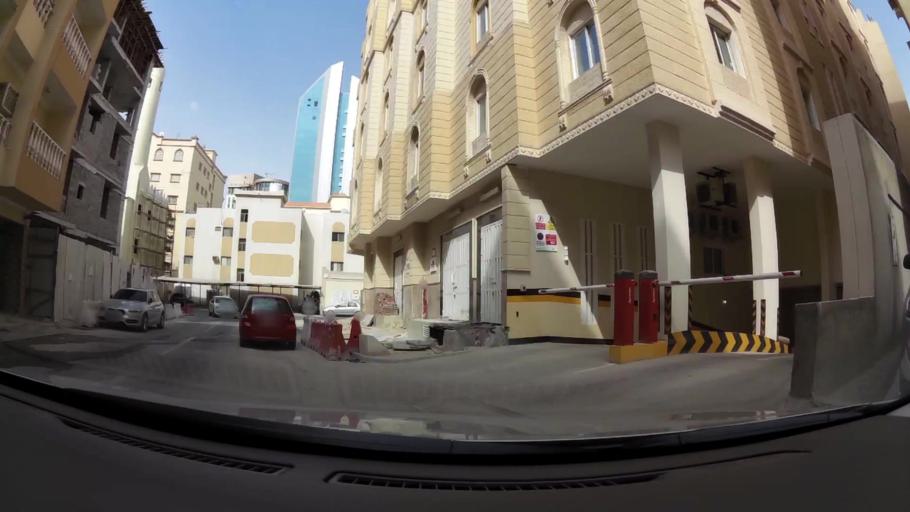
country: QA
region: Baladiyat ad Dawhah
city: Doha
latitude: 25.2866
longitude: 51.5085
